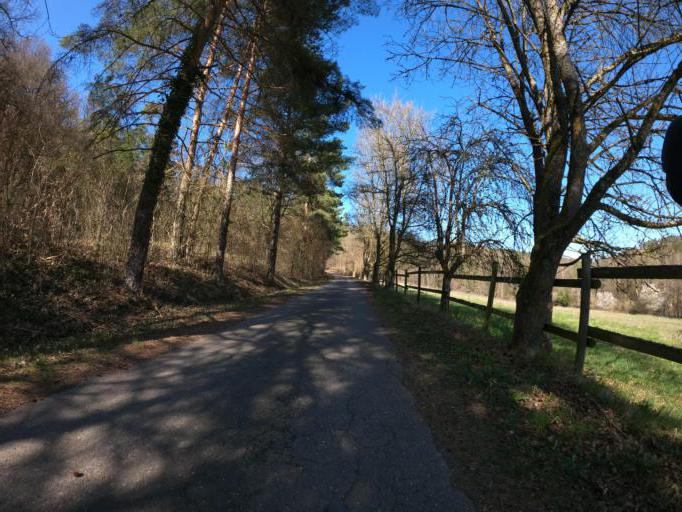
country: DE
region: Baden-Wuerttemberg
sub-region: Tuebingen Region
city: Rangendingen
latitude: 48.3876
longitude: 8.9032
